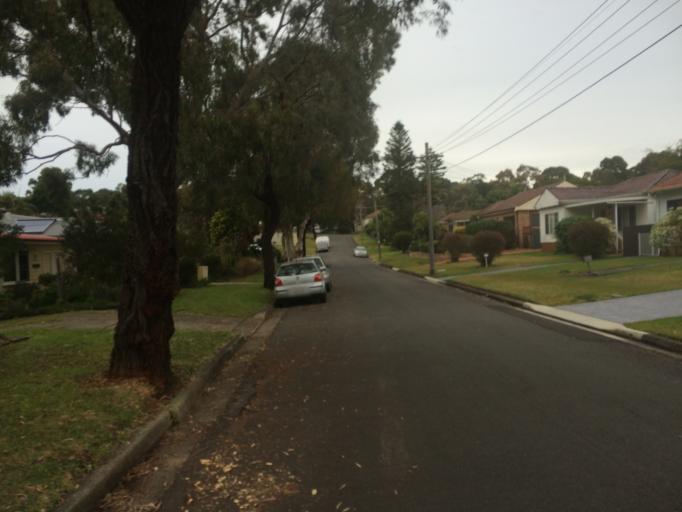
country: AU
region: New South Wales
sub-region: Sutherland Shire
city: Kirrawee
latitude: -34.0295
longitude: 151.0684
